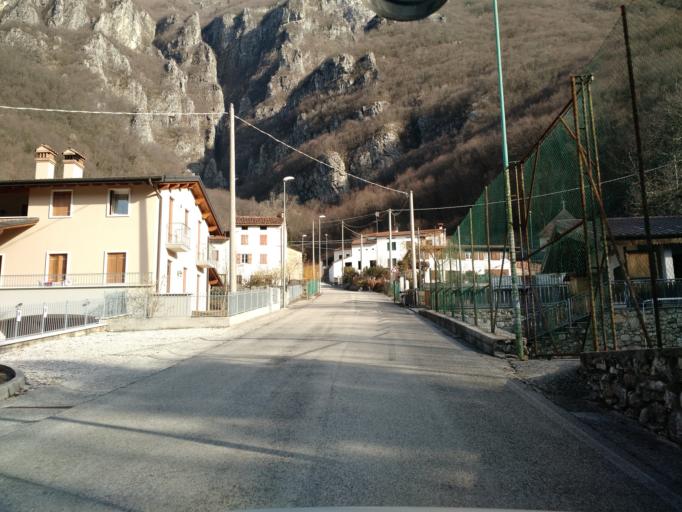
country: IT
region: Veneto
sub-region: Provincia di Vicenza
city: Velo d'Astico
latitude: 45.7968
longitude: 11.3972
